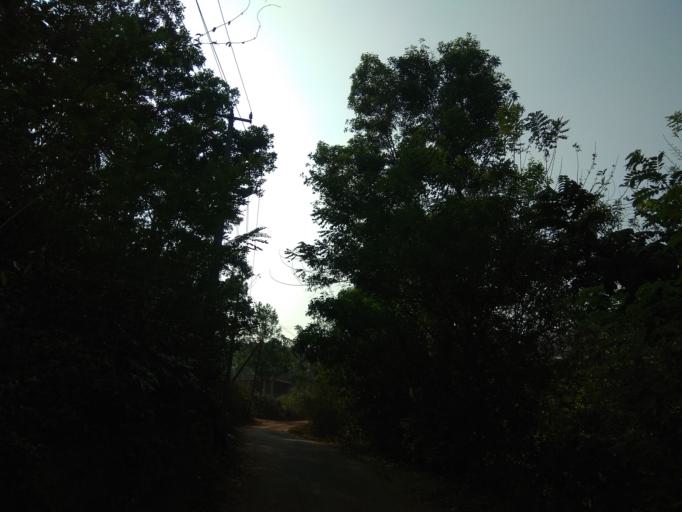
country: IN
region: Karnataka
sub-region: Dakshina Kannada
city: Mangalore
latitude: 12.9231
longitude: 74.8726
